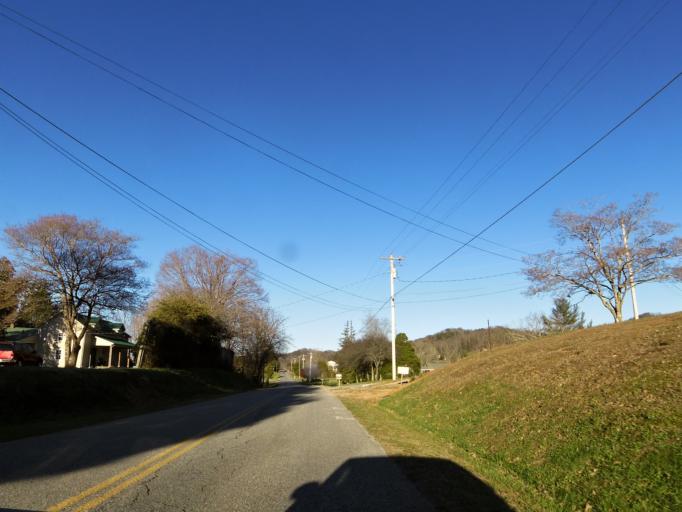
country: US
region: Tennessee
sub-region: Anderson County
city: Clinton
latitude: 36.1469
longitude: -84.1794
